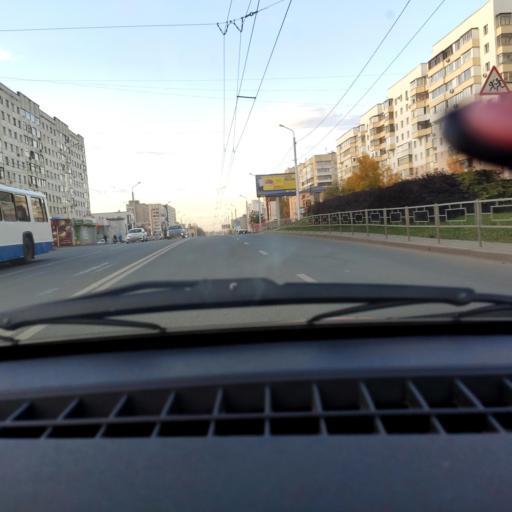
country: RU
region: Bashkortostan
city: Ufa
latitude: 54.7088
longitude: 55.9996
